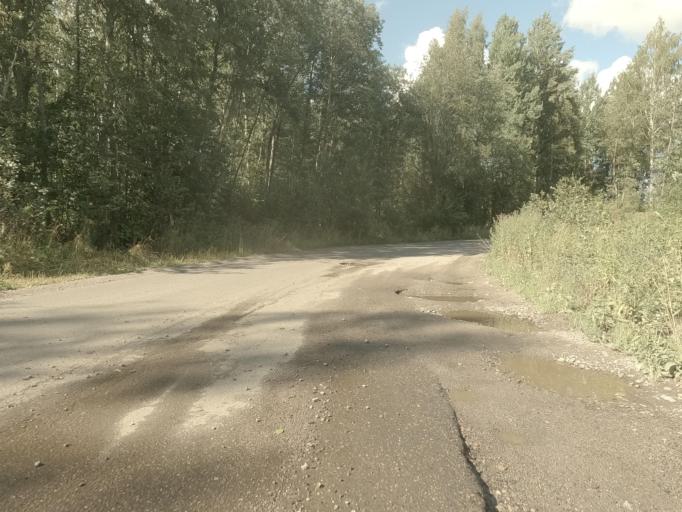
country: RU
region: Leningrad
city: Yanino Vtoroye
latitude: 59.9849
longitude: 30.6005
